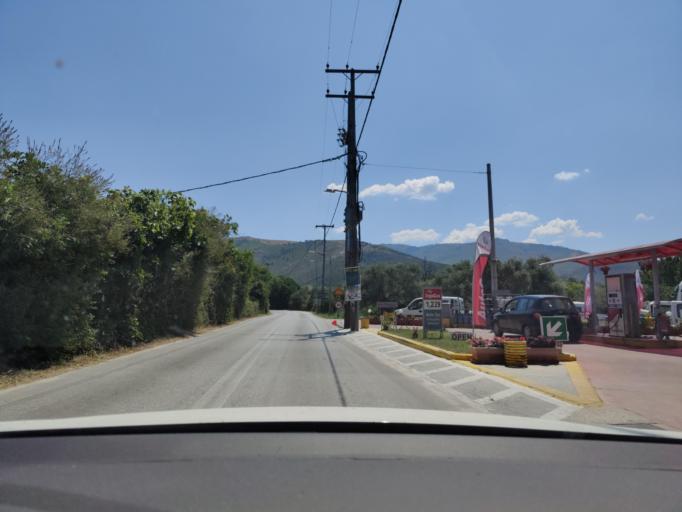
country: GR
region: East Macedonia and Thrace
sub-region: Nomos Kavalas
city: Prinos
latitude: 40.7572
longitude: 24.5775
